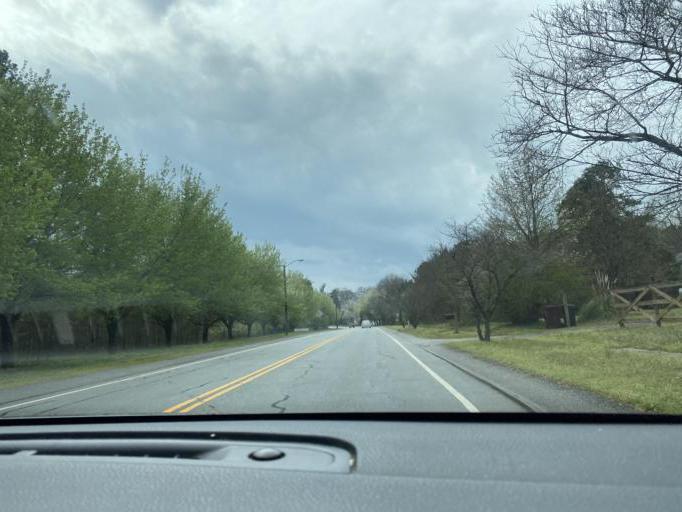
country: US
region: South Carolina
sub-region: Spartanburg County
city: Cowpens
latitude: 35.0226
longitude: -81.7933
